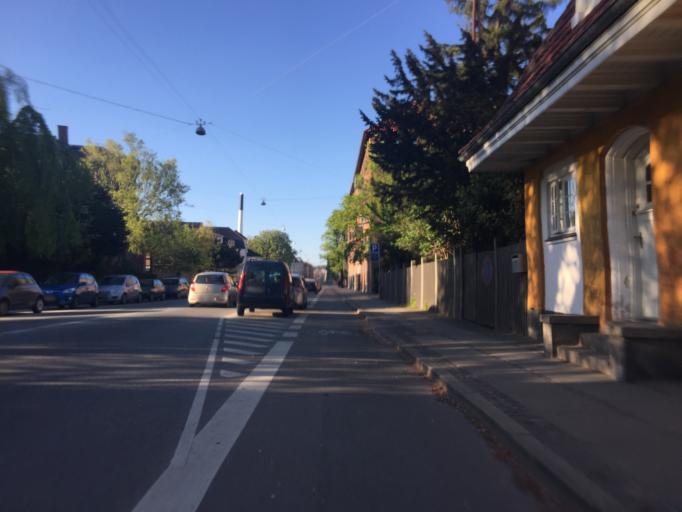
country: DK
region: Capital Region
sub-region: Frederiksberg Kommune
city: Frederiksberg
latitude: 55.6761
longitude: 12.5201
